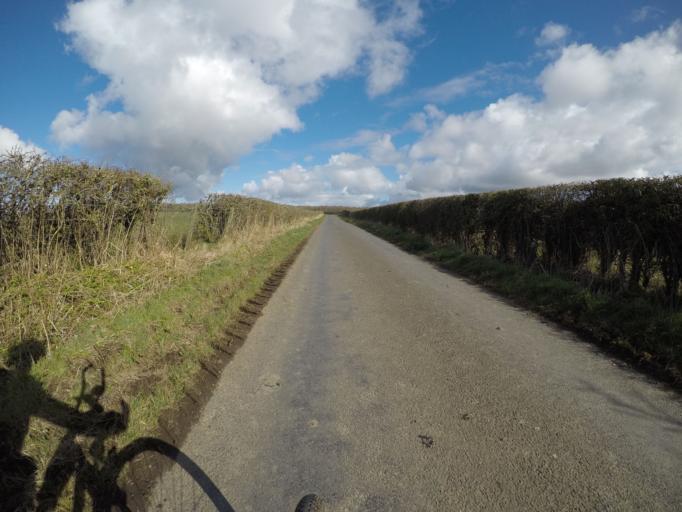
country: GB
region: Scotland
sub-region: North Ayrshire
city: Irvine
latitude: 55.6670
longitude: -4.6506
